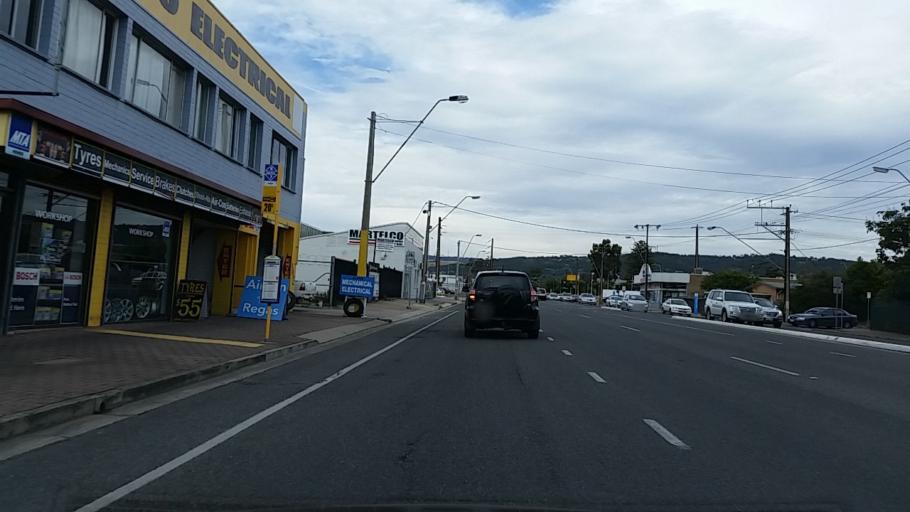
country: AU
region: South Australia
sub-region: Marion
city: Clovelly Park
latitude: -34.9928
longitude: 138.5730
